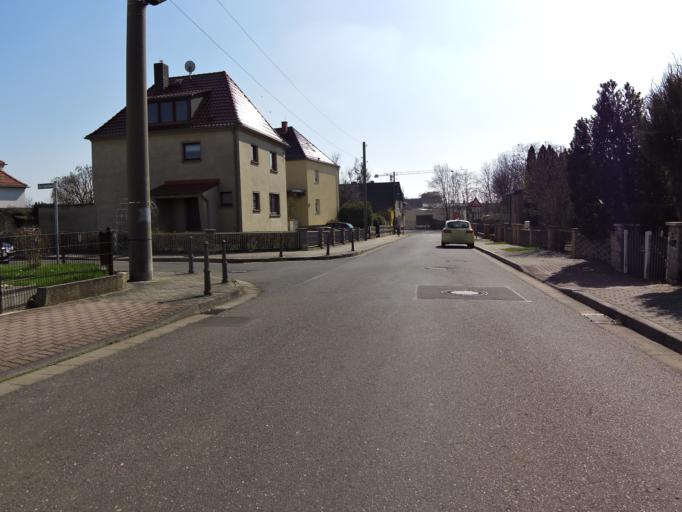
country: DE
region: Saxony
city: Leipzig
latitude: 51.3797
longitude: 12.3011
